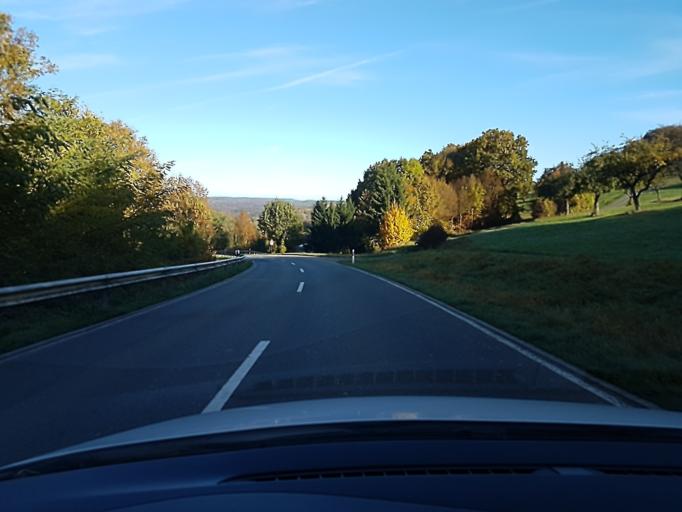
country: DE
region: Baden-Wuerttemberg
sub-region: Karlsruhe Region
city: Mosbach
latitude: 49.3756
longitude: 9.1948
